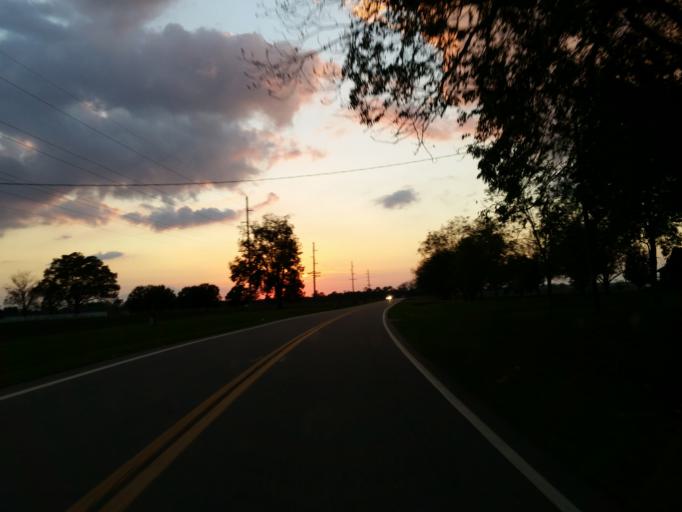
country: US
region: Georgia
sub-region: Dooly County
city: Vienna
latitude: 32.1318
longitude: -83.6997
